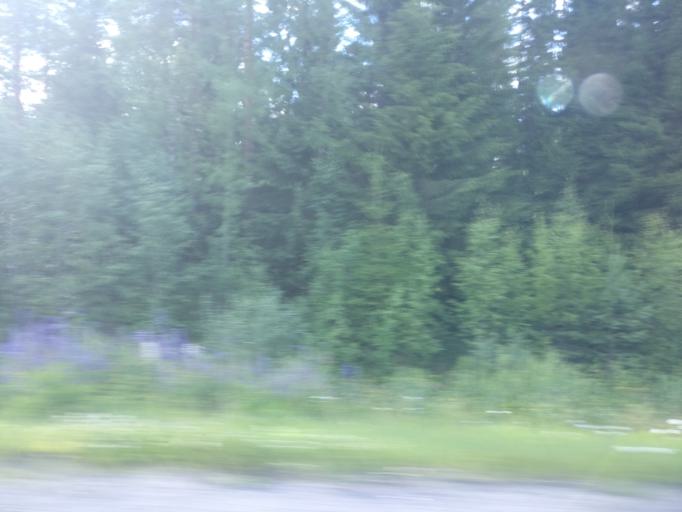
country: FI
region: Uusimaa
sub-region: Helsinki
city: Hyvinge
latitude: 60.6014
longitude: 24.8624
